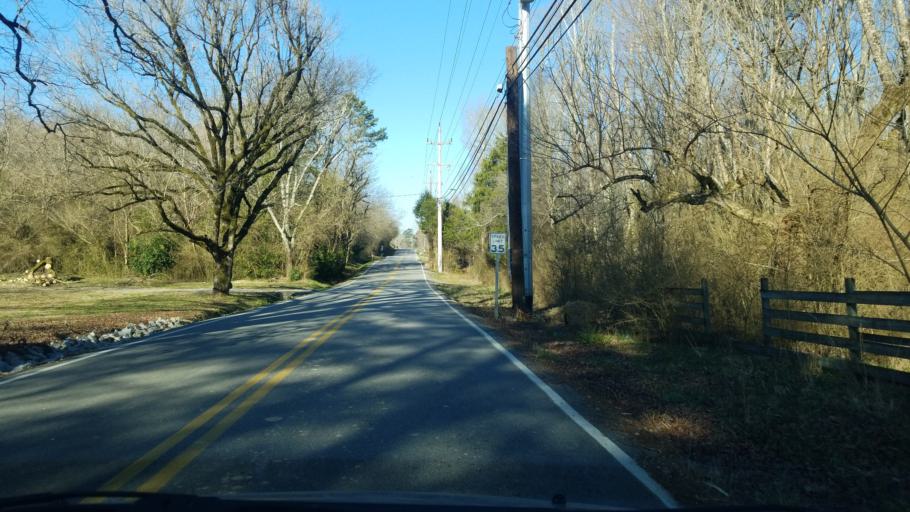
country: US
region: Tennessee
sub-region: Hamilton County
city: Collegedale
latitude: 35.0369
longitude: -85.0869
